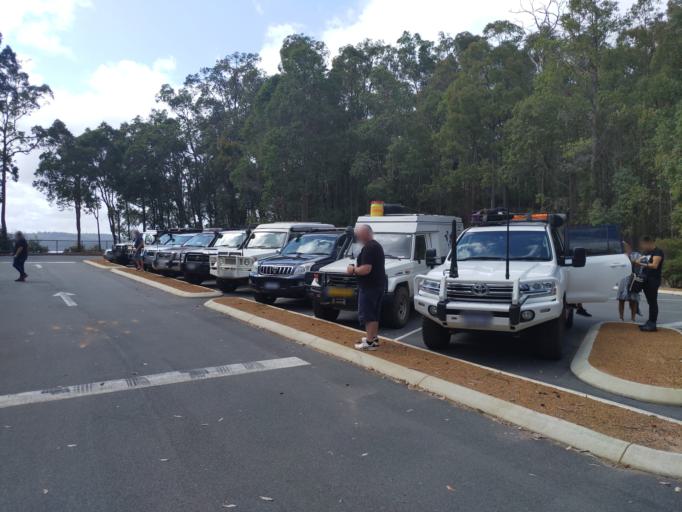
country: AU
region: Western Australia
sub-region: Serpentine-Jarrahdale
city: Serpentine
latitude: -32.4057
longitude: 116.0979
